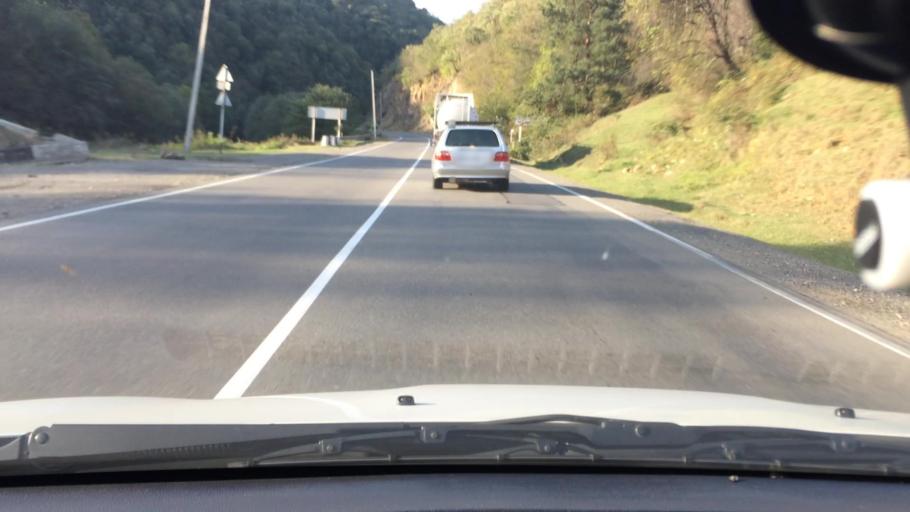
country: GE
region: Imereti
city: Kharagauli
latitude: 42.1081
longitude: 43.2488
